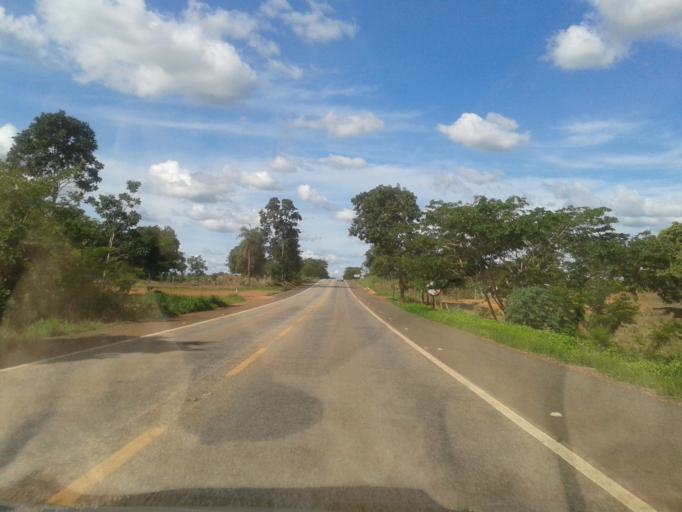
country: BR
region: Goias
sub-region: Mozarlandia
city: Mozarlandia
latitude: -15.0758
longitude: -50.6204
